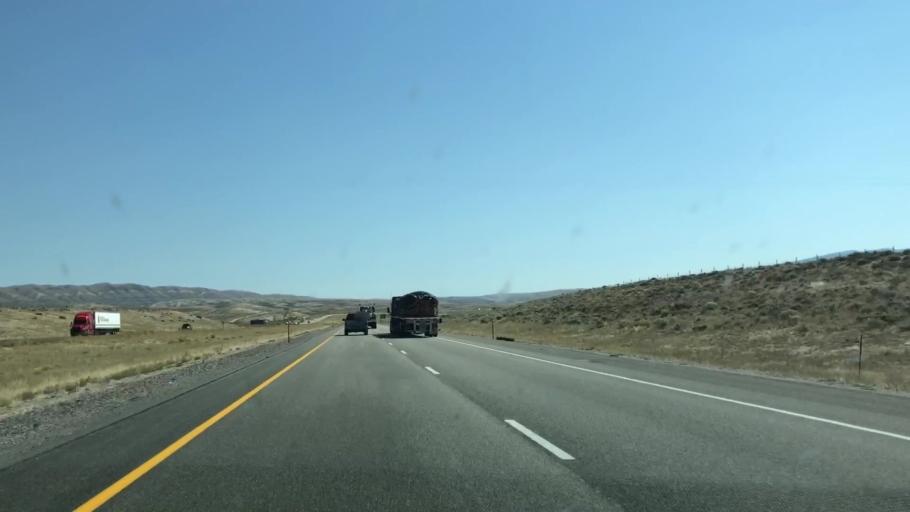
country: US
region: Wyoming
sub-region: Carbon County
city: Saratoga
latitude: 41.7413
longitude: -106.7900
